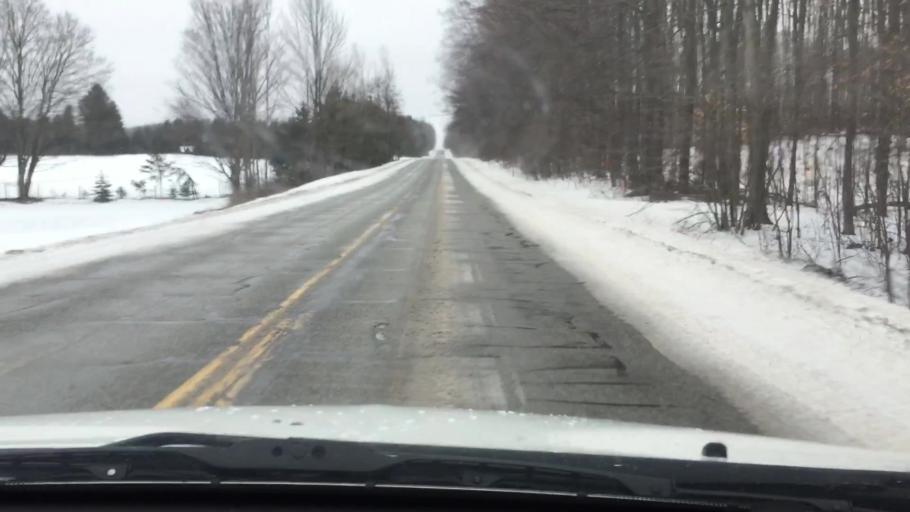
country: US
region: Michigan
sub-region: Wexford County
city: Cadillac
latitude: 44.1911
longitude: -85.4057
